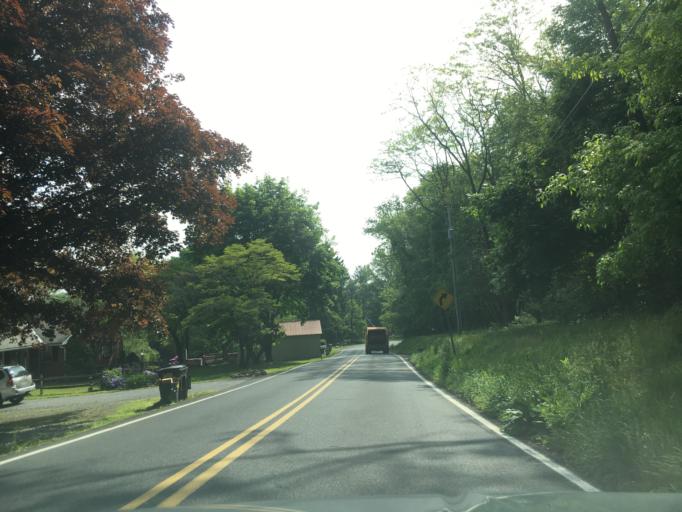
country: US
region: Pennsylvania
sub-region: Berks County
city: New Berlinville
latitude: 40.3466
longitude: -75.6378
